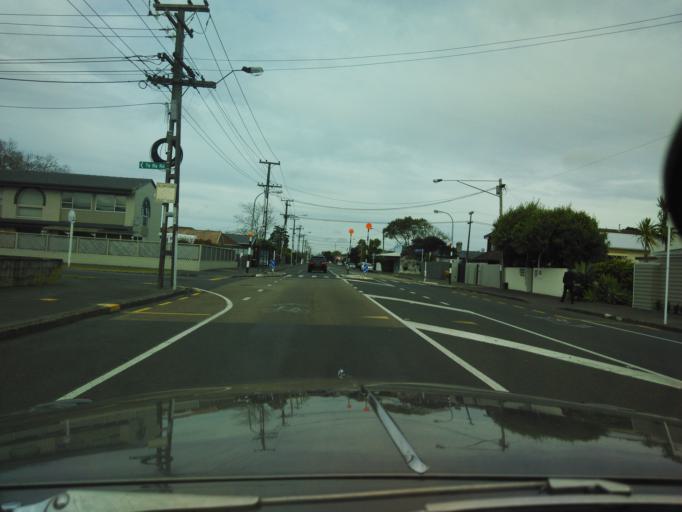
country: NZ
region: Auckland
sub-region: Auckland
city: Rosebank
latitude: -36.8606
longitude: 174.7028
